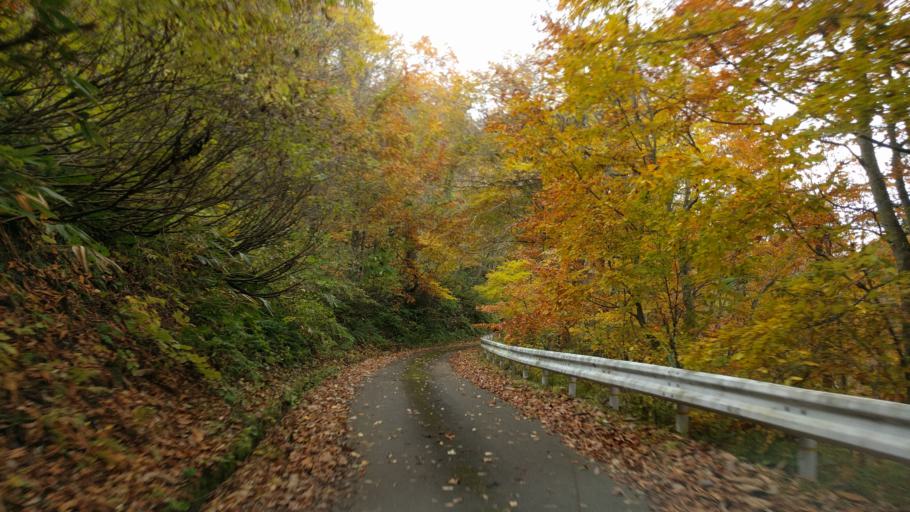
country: JP
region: Fukushima
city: Kitakata
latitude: 37.3876
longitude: 139.7184
